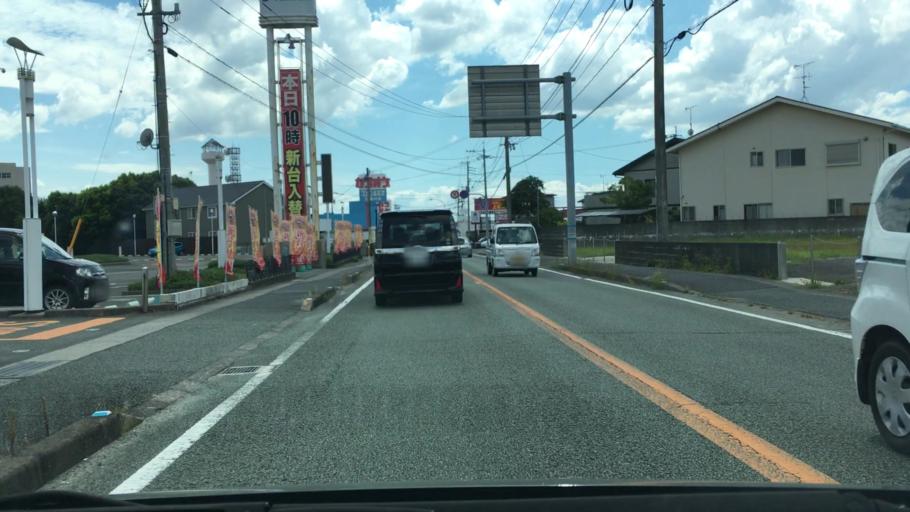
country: JP
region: Saga Prefecture
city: Kanzakimachi-kanzaki
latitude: 33.3302
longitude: 130.4118
